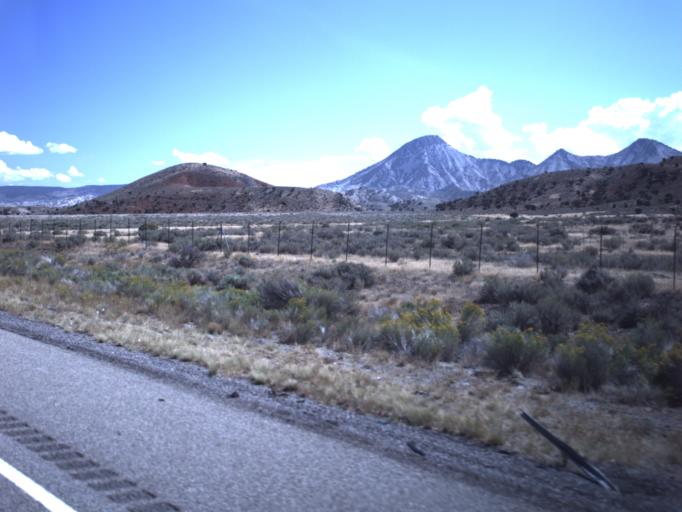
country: US
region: Utah
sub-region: Sevier County
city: Aurora
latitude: 38.8815
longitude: -111.9244
